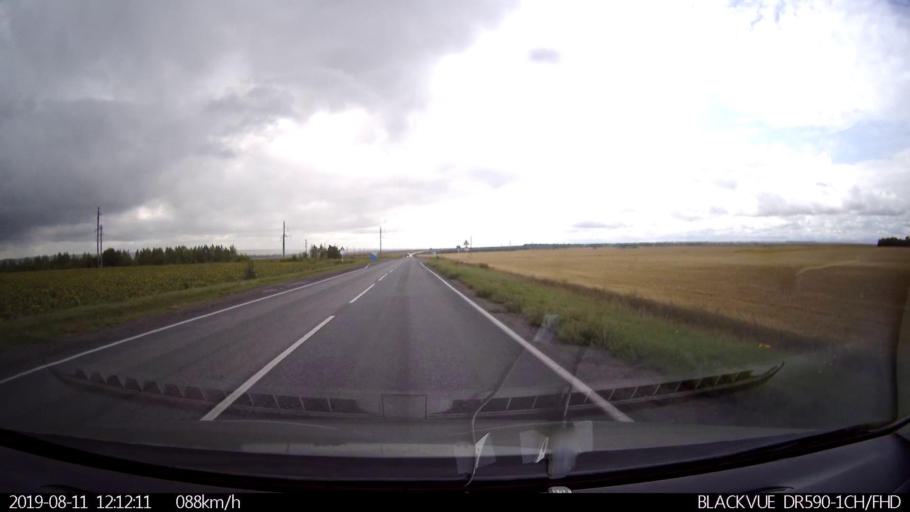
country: RU
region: Ulyanovsk
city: Silikatnyy
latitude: 53.9765
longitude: 47.9978
